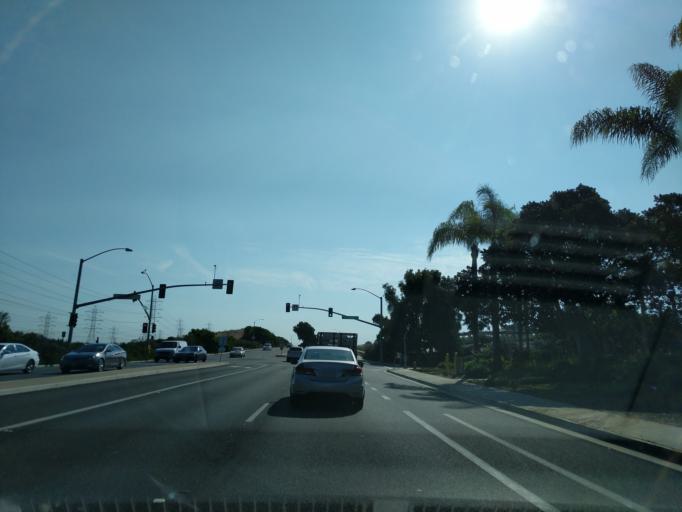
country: US
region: California
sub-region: San Diego County
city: Carlsbad
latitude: 33.1353
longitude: -117.3236
